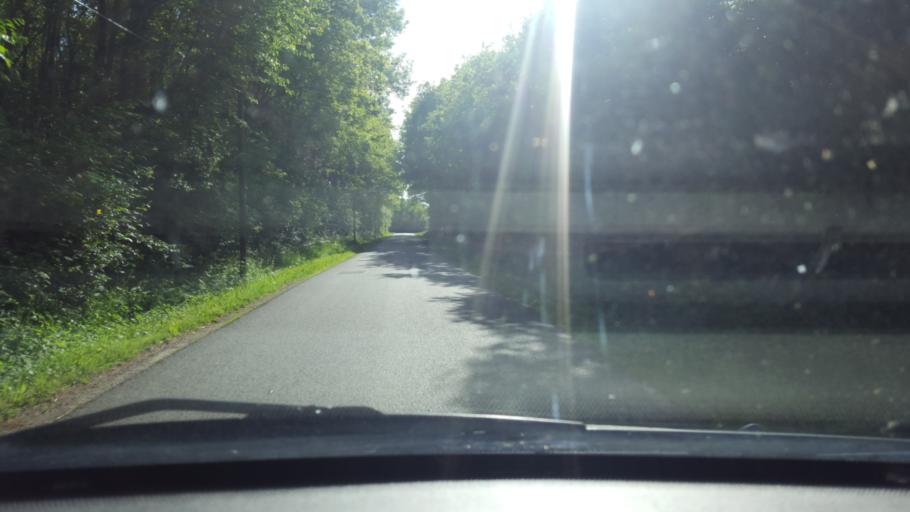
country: FR
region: Pays de la Loire
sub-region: Departement de la Loire-Atlantique
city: La Chevroliere
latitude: 47.0491
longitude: -1.5897
